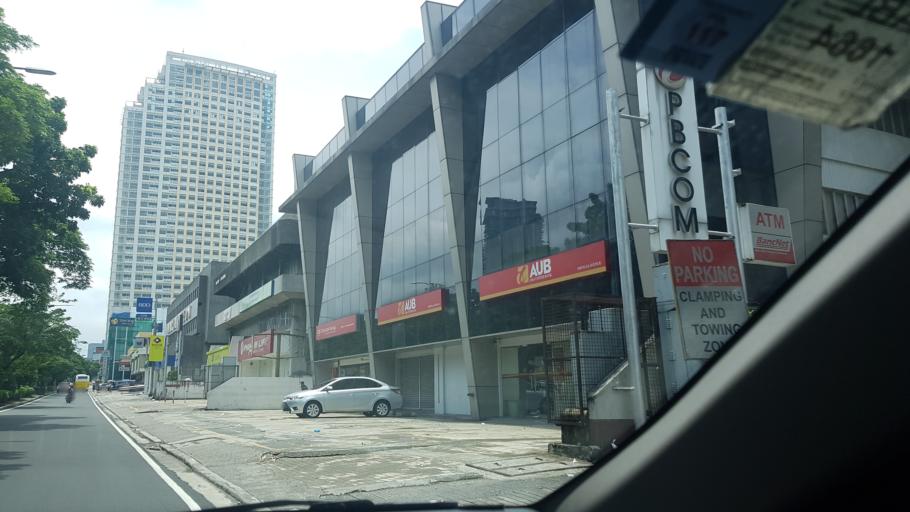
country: PH
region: Metro Manila
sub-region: San Juan
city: San Juan
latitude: 14.6026
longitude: 121.0455
